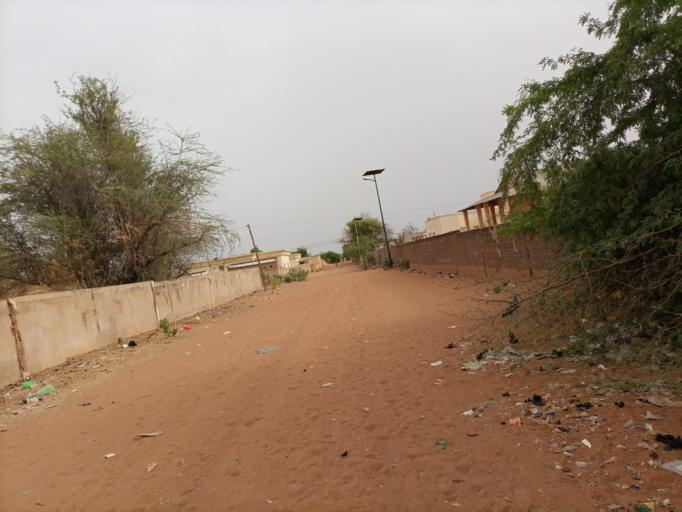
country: SN
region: Louga
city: Ndibene Dahra
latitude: 15.3979
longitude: -15.1145
